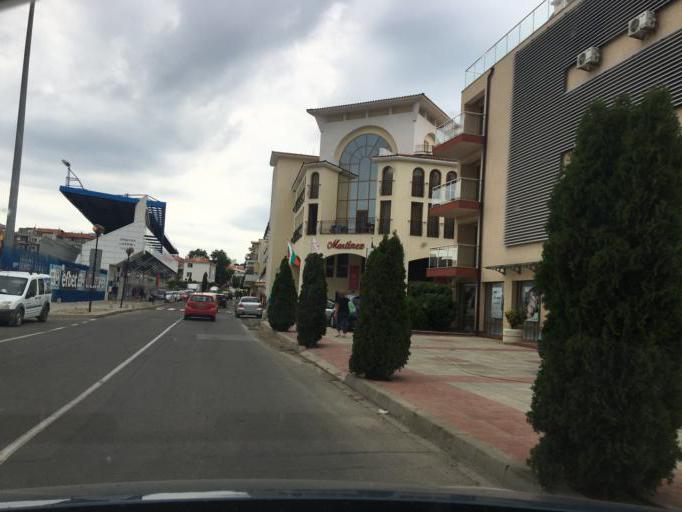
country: BG
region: Burgas
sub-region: Obshtina Sozopol
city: Sozopol
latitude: 42.4129
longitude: 27.6980
